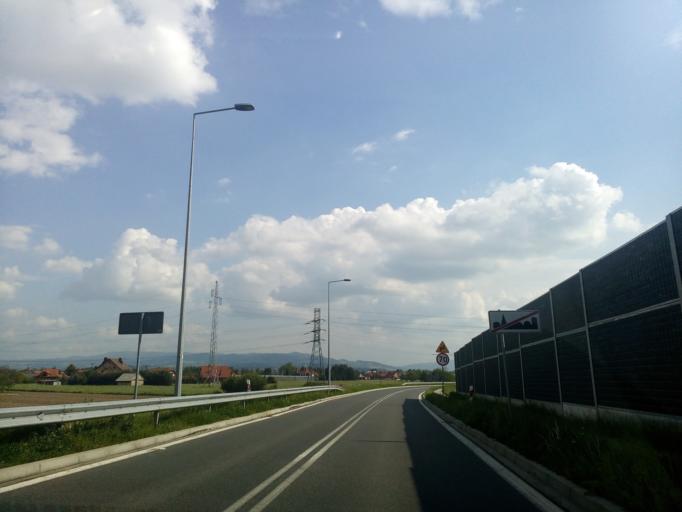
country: PL
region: Lesser Poland Voivodeship
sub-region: Powiat nowosadecki
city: Chelmiec
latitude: 49.6301
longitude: 20.6521
